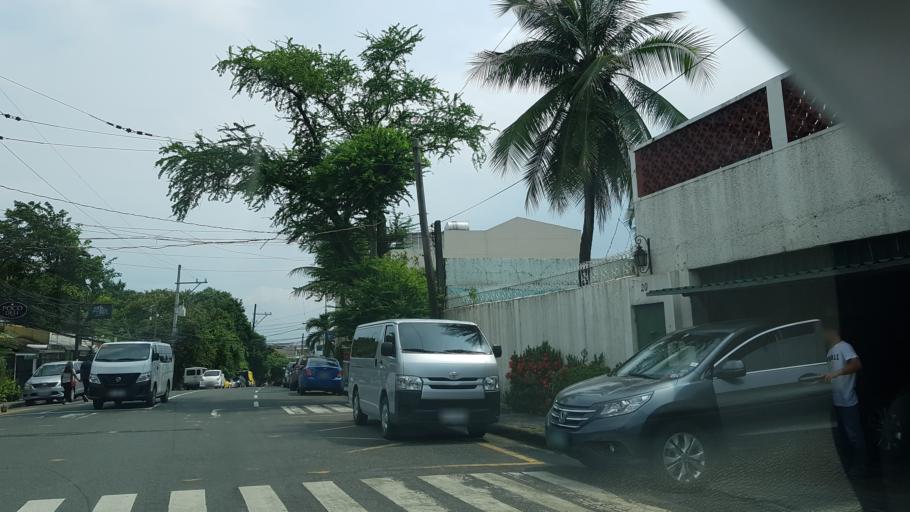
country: PH
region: Metro Manila
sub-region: Pasig
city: Pasig City
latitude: 14.5714
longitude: 121.0608
